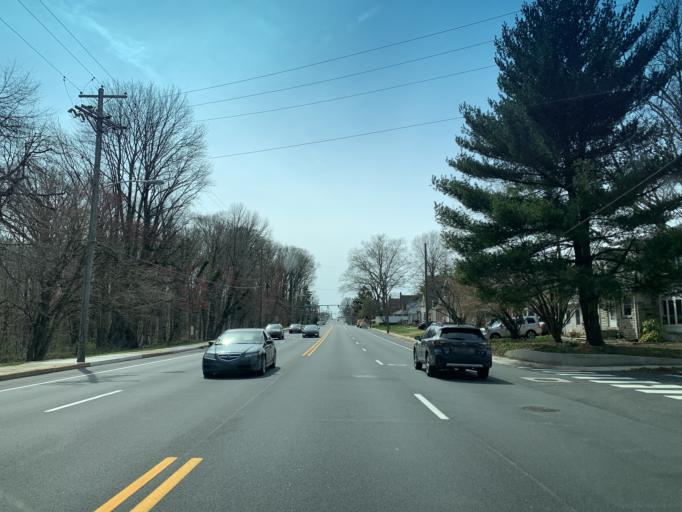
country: US
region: Delaware
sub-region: New Castle County
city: Newport
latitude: 39.7205
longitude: -75.5975
